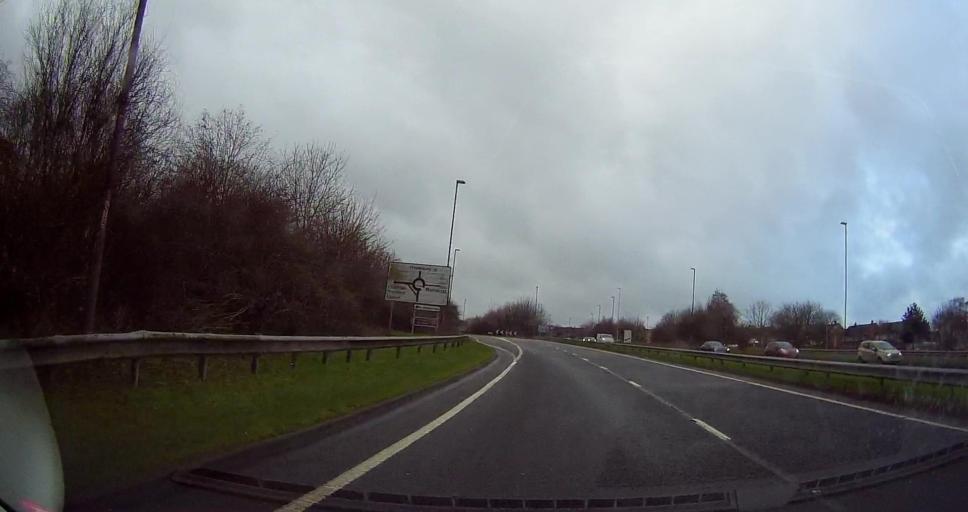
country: GB
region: England
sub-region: Medway
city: Rochester
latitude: 51.4078
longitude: 0.5118
